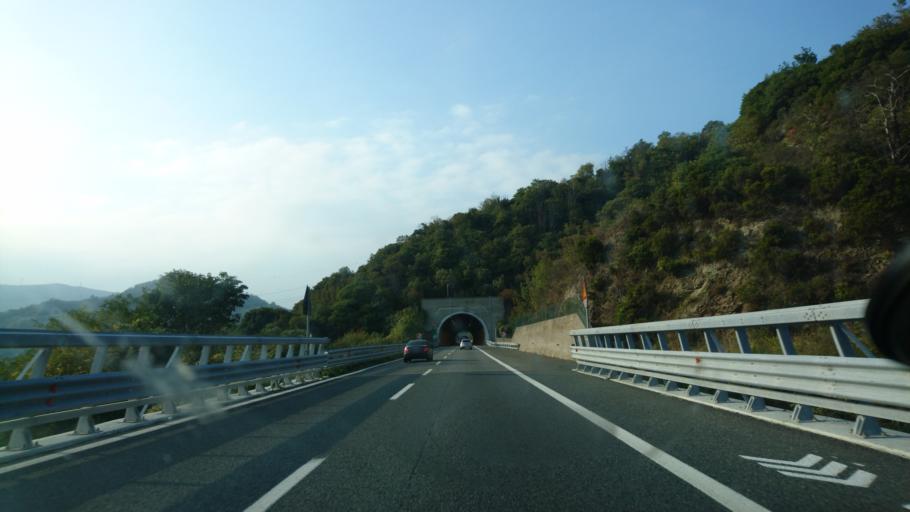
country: IT
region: Liguria
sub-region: Provincia di Savona
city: Quiliano
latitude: 44.3140
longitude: 8.3958
